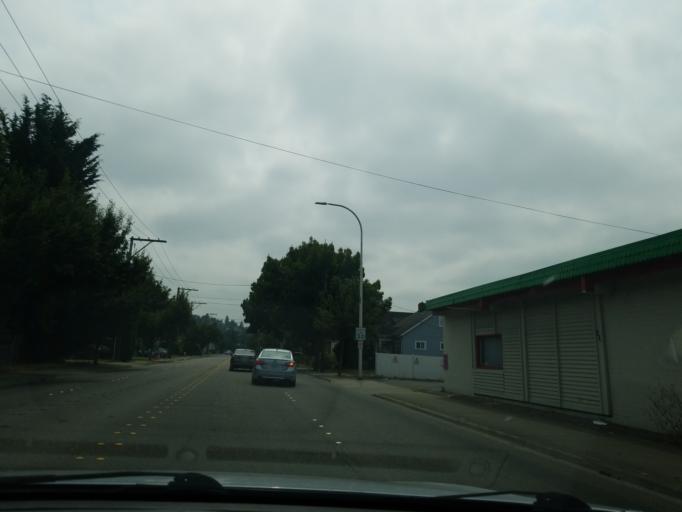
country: US
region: Washington
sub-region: King County
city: Renton
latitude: 47.4865
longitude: -122.2022
